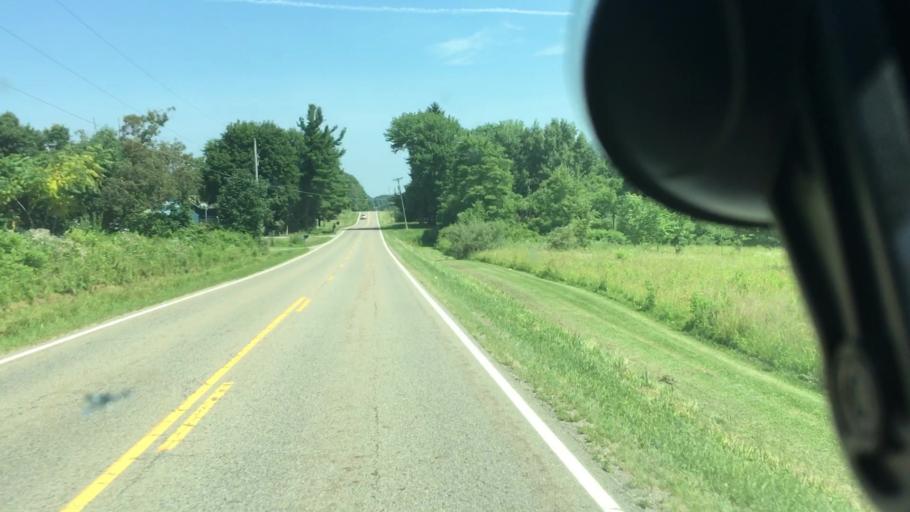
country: US
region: Ohio
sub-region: Columbiana County
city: Salem
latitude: 40.8054
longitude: -80.8584
